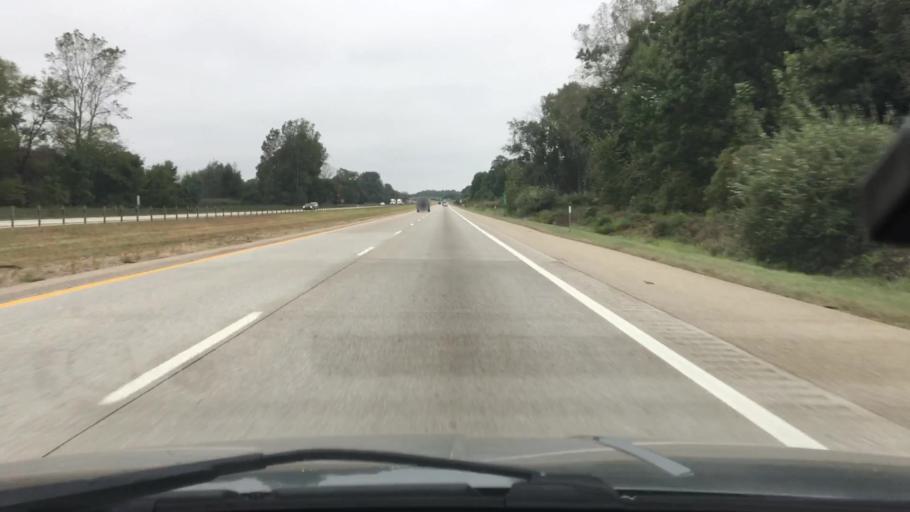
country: US
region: Michigan
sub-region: Van Buren County
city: Paw Paw
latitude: 42.2049
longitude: -85.9289
